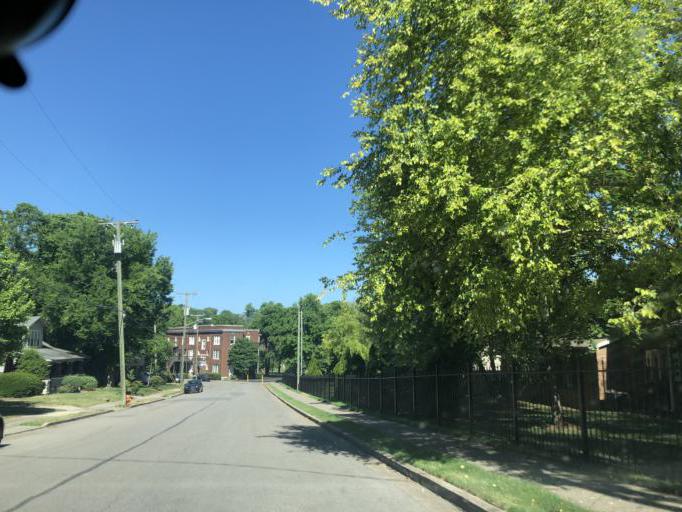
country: US
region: Tennessee
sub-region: Davidson County
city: Nashville
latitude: 36.1292
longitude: -86.7934
